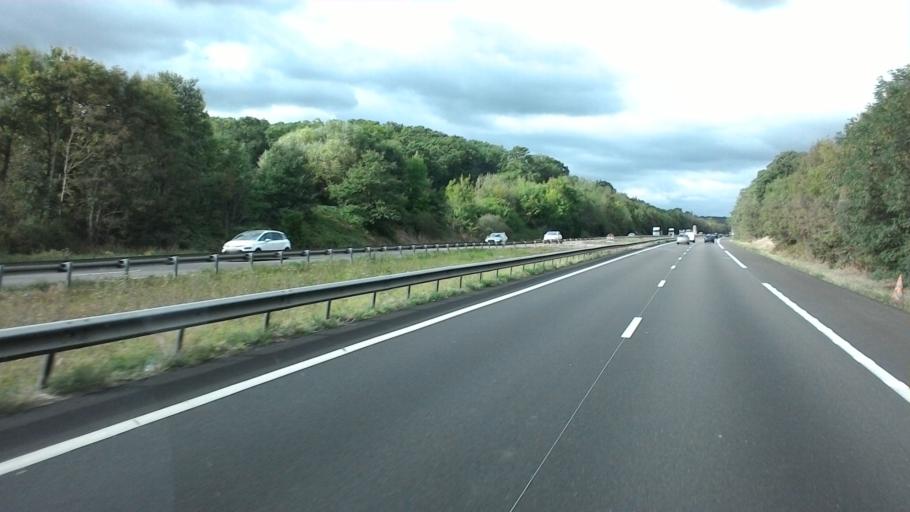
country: FR
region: Lorraine
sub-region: Departement de Meurthe-et-Moselle
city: Pont-a-Mousson
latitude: 48.9662
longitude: 6.1061
